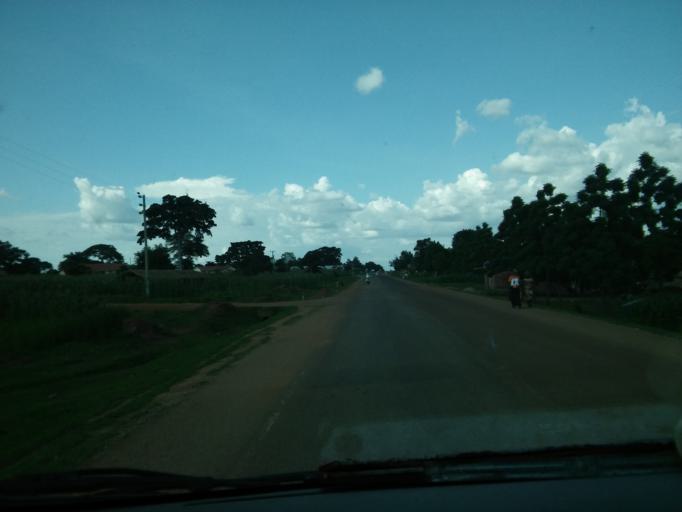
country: UG
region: Eastern Region
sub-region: Kibuku District
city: Kibuku
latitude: 1.0046
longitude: 33.7718
